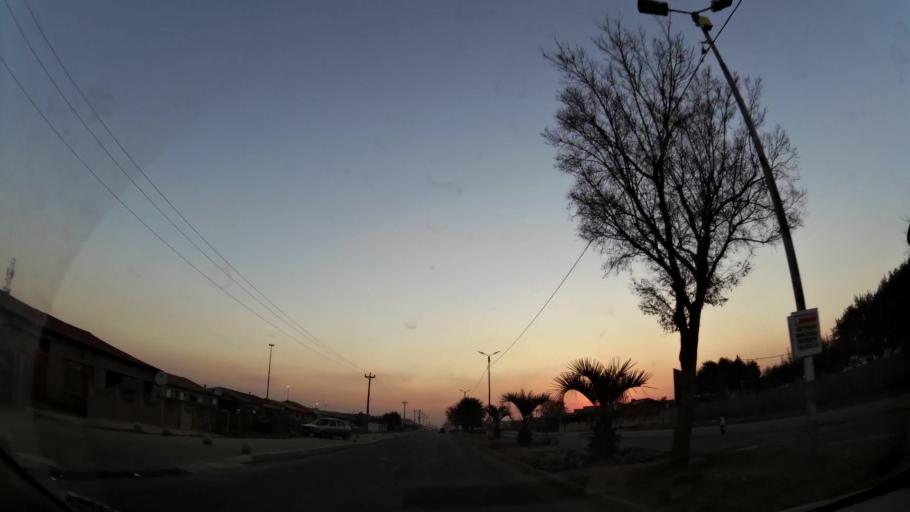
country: ZA
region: Gauteng
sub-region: Ekurhuleni Metropolitan Municipality
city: Nigel
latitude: -26.3755
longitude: 28.4124
